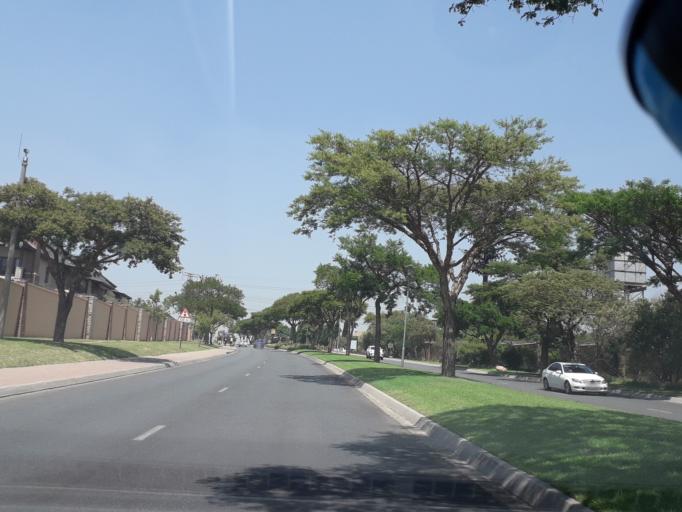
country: ZA
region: Gauteng
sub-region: City of Johannesburg Metropolitan Municipality
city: Midrand
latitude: -26.0285
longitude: 28.0813
